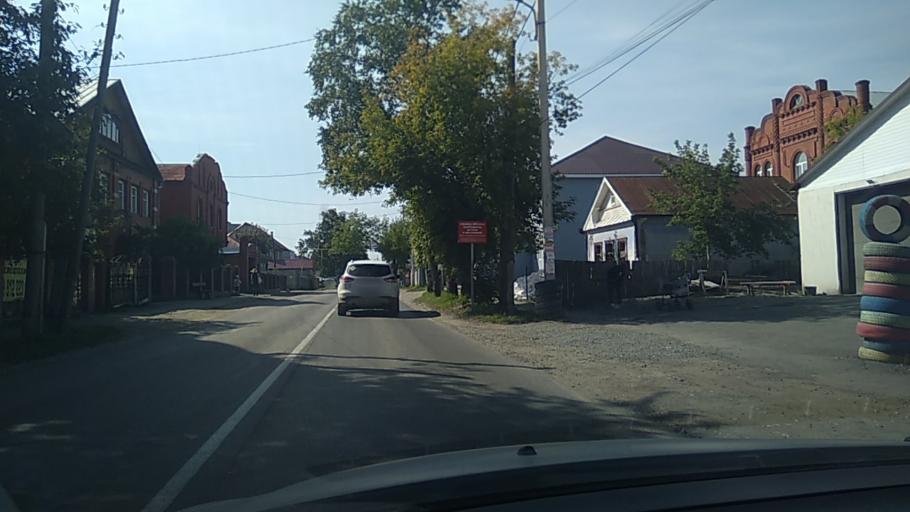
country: RU
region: Sverdlovsk
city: Sovkhoznyy
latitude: 56.8086
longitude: 60.5752
